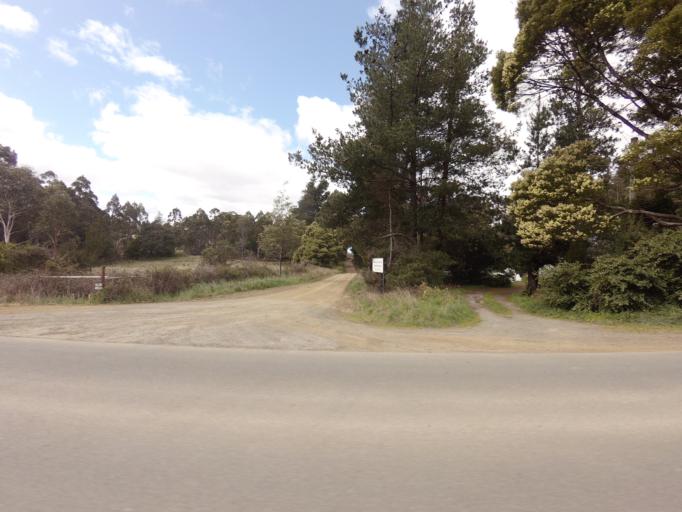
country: AU
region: Tasmania
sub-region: Huon Valley
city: Geeveston
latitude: -43.3334
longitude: 146.9712
